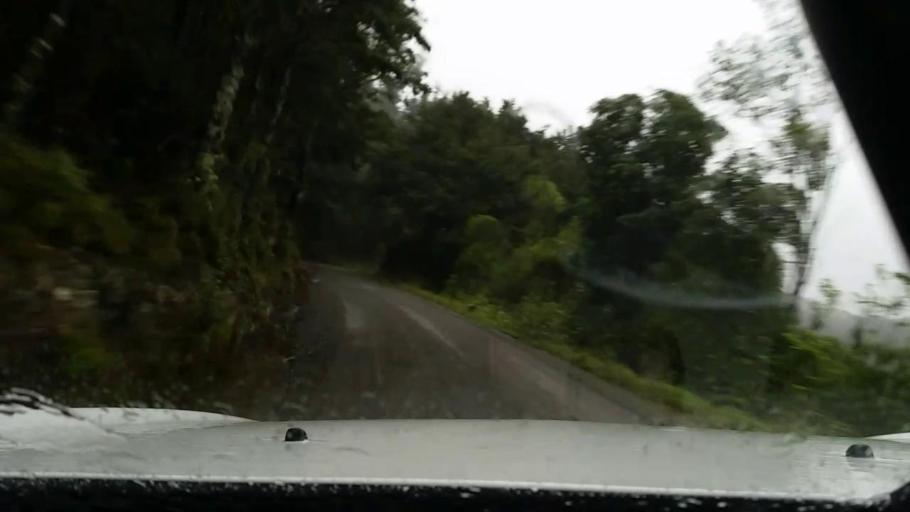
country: NZ
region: Wellington
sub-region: Masterton District
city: Masterton
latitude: -41.1870
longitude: 175.8185
